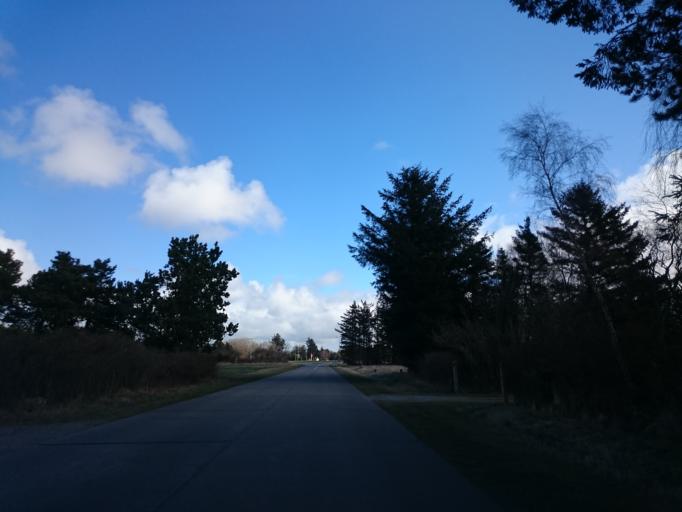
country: DK
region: North Denmark
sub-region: Frederikshavn Kommune
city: Skagen
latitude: 57.6570
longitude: 10.4544
